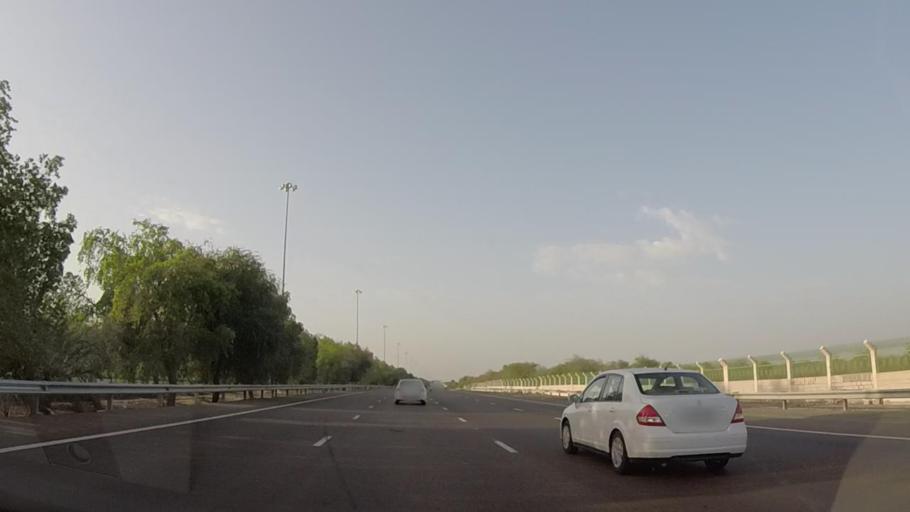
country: AE
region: Dubai
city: Dubai
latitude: 24.7678
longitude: 54.8475
